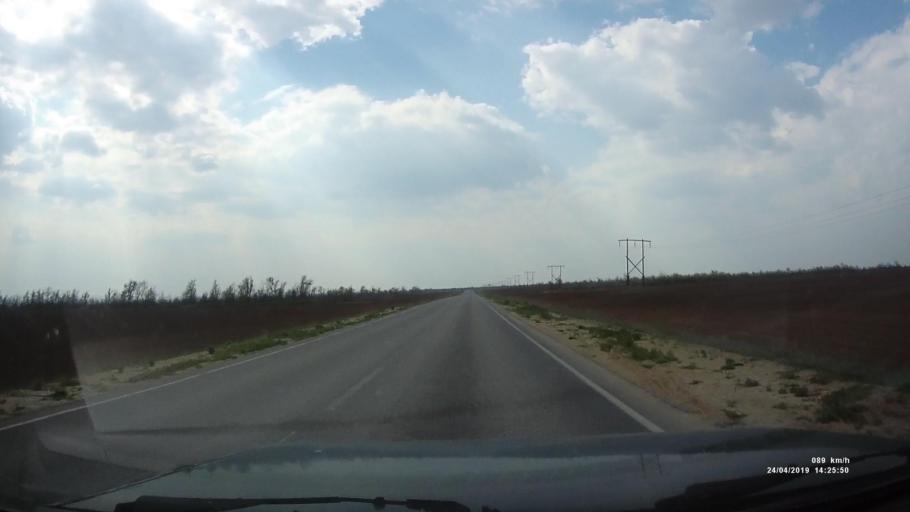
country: RU
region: Kalmykiya
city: Arshan'
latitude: 46.3321
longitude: 44.0742
